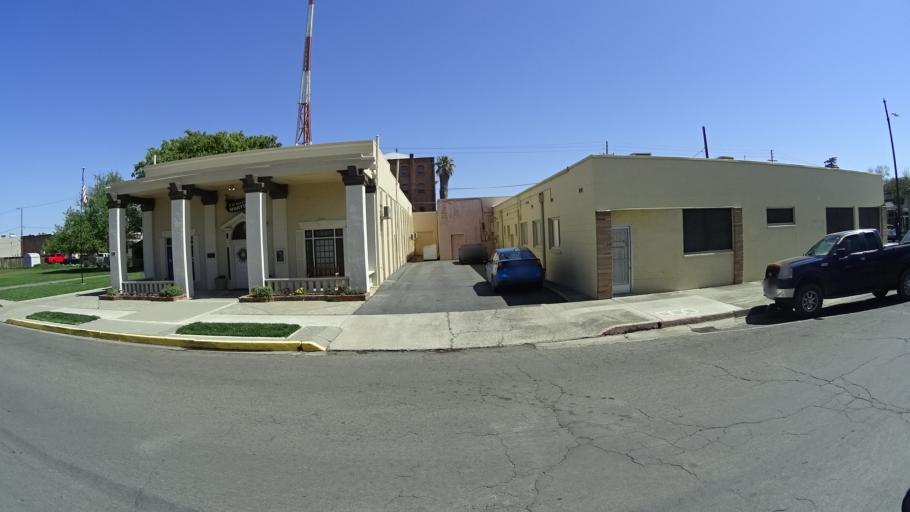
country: US
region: California
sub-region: Glenn County
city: Willows
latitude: 39.5208
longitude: -122.1968
